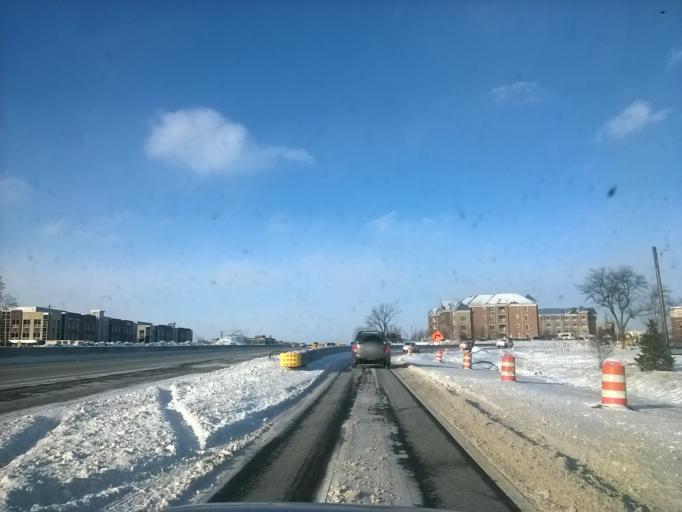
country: US
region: Indiana
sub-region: Hamilton County
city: Carmel
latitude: 39.9648
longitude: -86.1575
